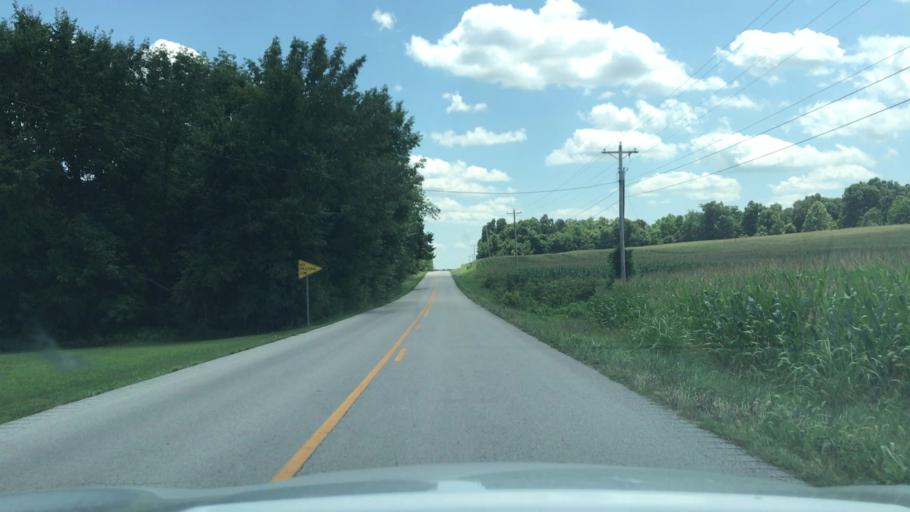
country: US
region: Kentucky
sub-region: Christian County
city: Hopkinsville
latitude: 36.9937
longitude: -87.3633
